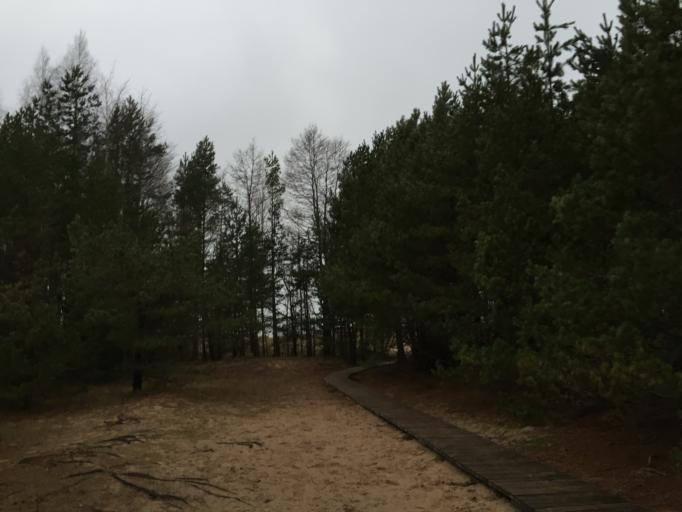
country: EE
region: Saare
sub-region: Kuressaare linn
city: Kuressaare
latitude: 58.5923
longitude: 22.5030
